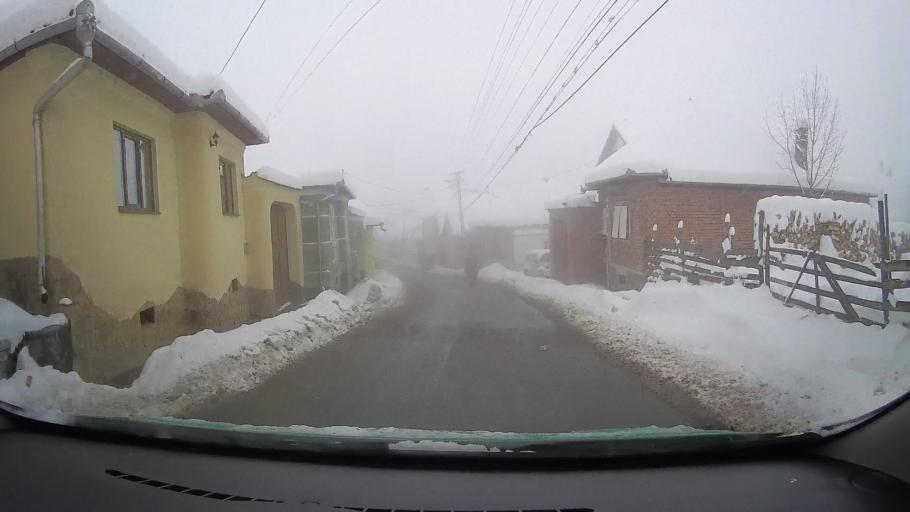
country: RO
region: Sibiu
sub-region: Comuna Jina
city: Jina
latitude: 45.7850
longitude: 23.6780
